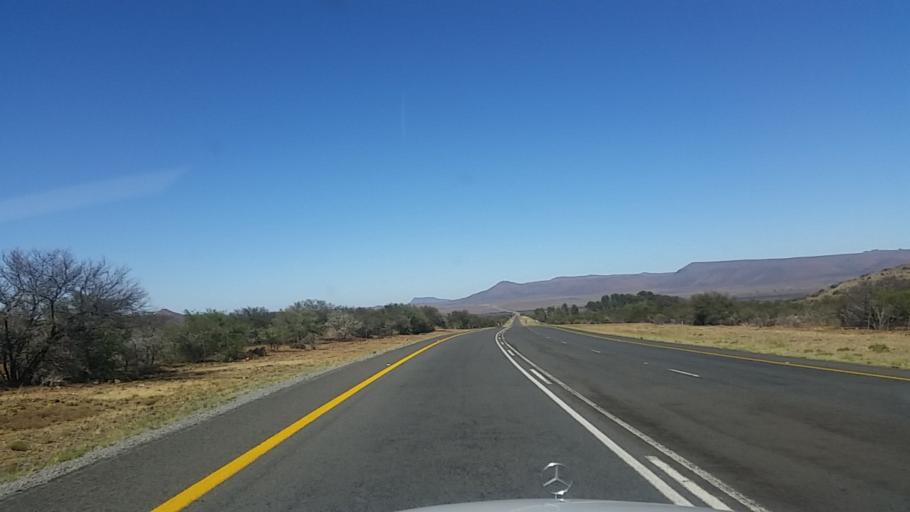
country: ZA
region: Eastern Cape
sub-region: Cacadu District Municipality
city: Graaff-Reinet
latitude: -31.9752
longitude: 24.7094
